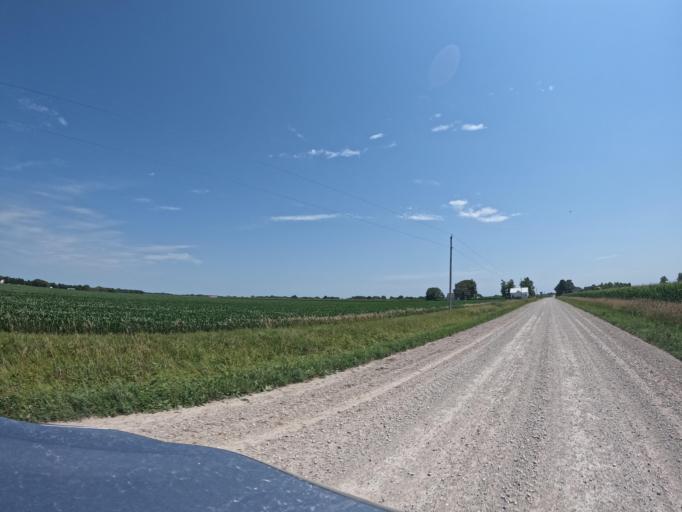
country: US
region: Iowa
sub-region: Henry County
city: Mount Pleasant
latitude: 40.9033
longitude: -91.6316
